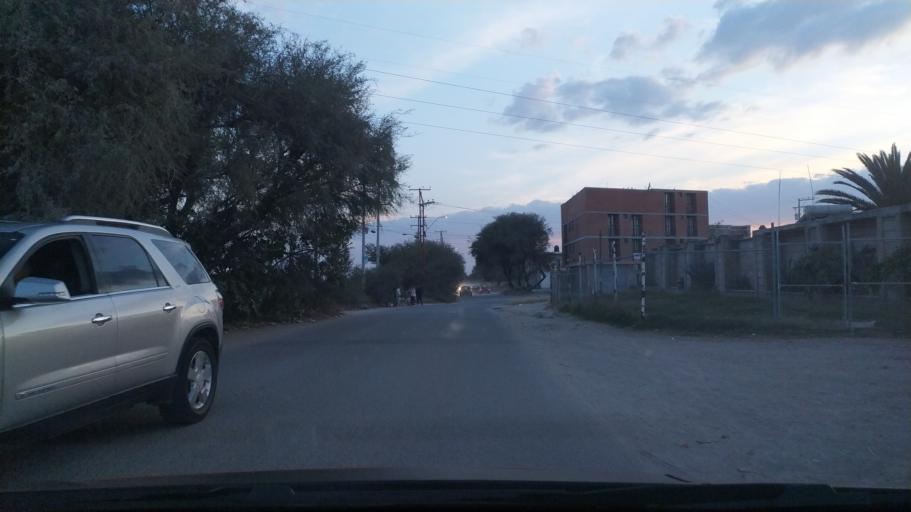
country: MX
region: Guanajuato
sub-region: San Francisco del Rincon
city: Estacion de San Francisco
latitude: 21.0394
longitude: -101.8443
